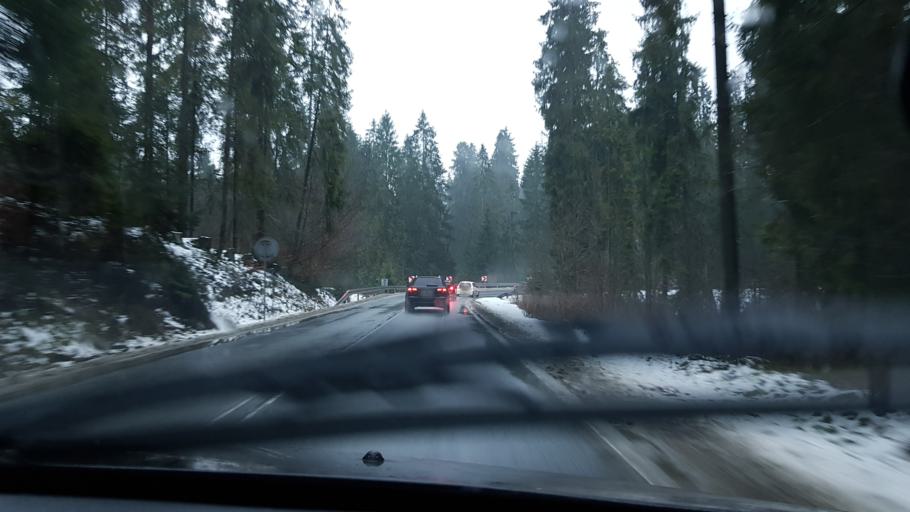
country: PL
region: Lesser Poland Voivodeship
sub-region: Powiat nowotarski
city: Sieniawa
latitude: 49.5148
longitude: 19.8968
